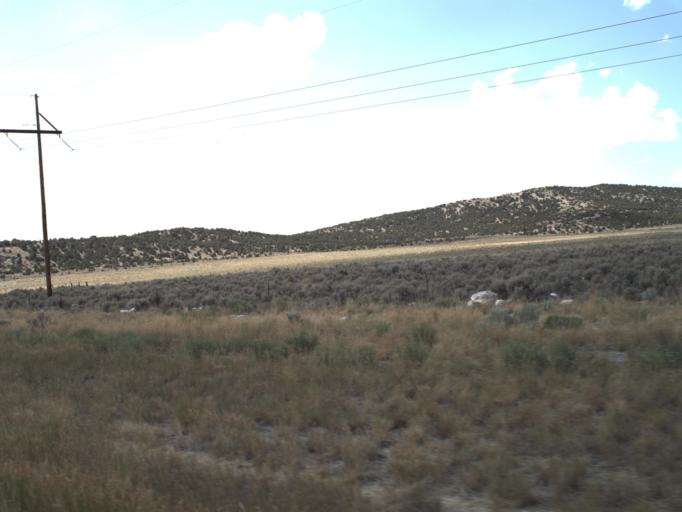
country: US
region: Idaho
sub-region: Minidoka County
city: Rupert
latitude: 41.9715
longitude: -113.1402
